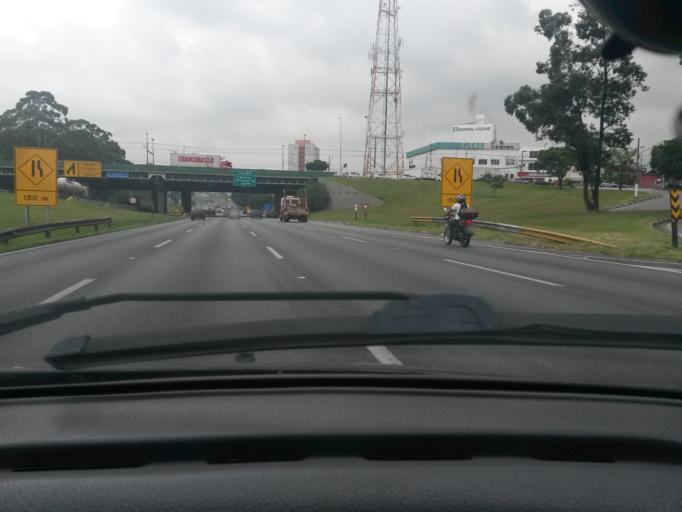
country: BR
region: Sao Paulo
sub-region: Sao Bernardo Do Campo
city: Sao Bernardo do Campo
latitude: -23.6886
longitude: -46.5655
